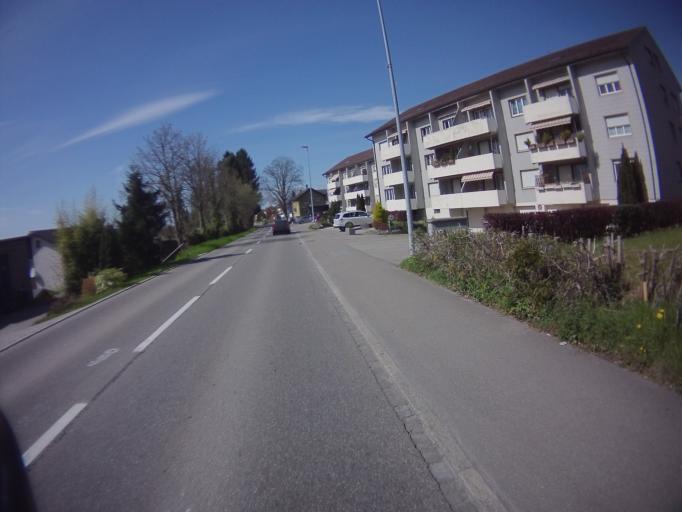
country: CH
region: Aargau
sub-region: Bezirk Baden
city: Niederrohrdorf
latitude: 47.4198
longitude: 8.3159
